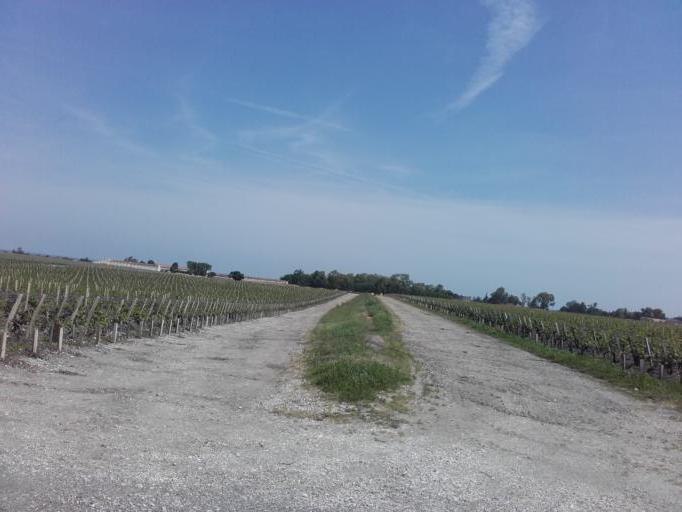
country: FR
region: Aquitaine
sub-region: Departement de la Gironde
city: Pauillac
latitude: 45.2140
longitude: -0.7807
